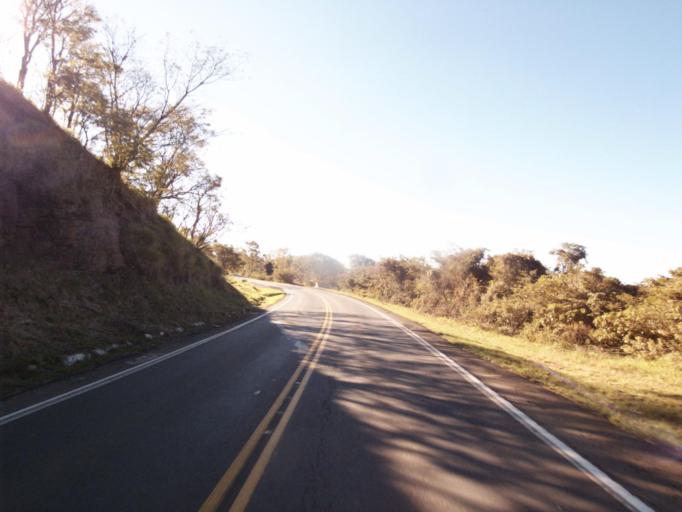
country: AR
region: Misiones
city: Bernardo de Irigoyen
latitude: -26.4942
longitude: -53.5015
